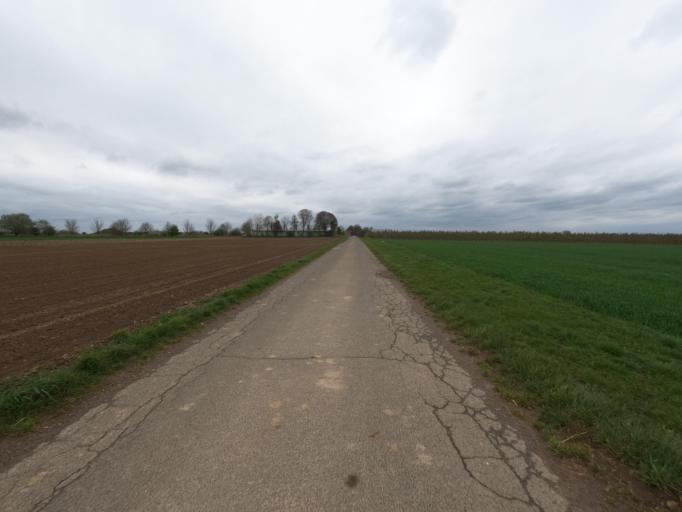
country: DE
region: North Rhine-Westphalia
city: Baesweiler
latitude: 50.9745
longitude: 6.1891
